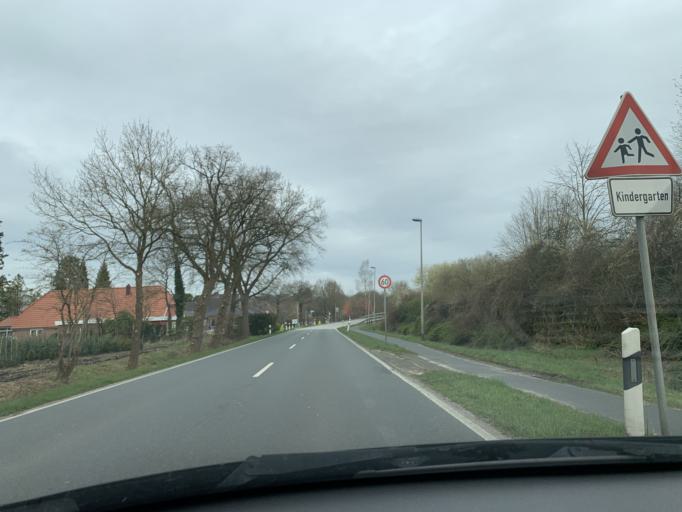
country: DE
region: Lower Saxony
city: Bad Zwischenahn
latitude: 53.1833
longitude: 7.9829
